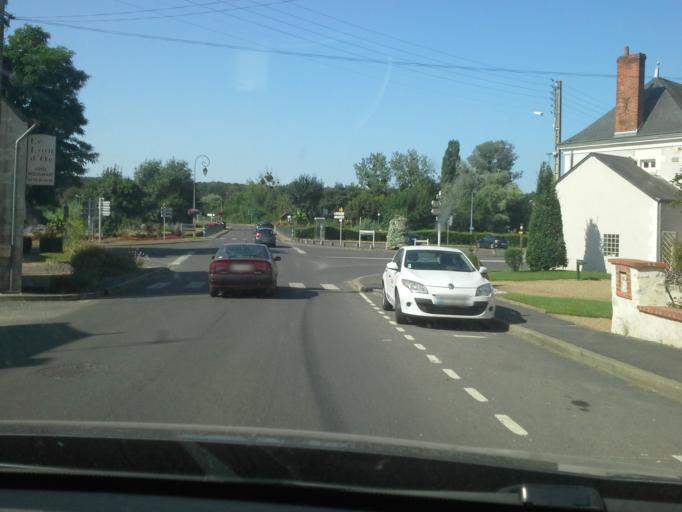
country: FR
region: Centre
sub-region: Departement du Loir-et-Cher
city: Cande-sur-Beuvron
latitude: 47.4948
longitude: 1.2612
